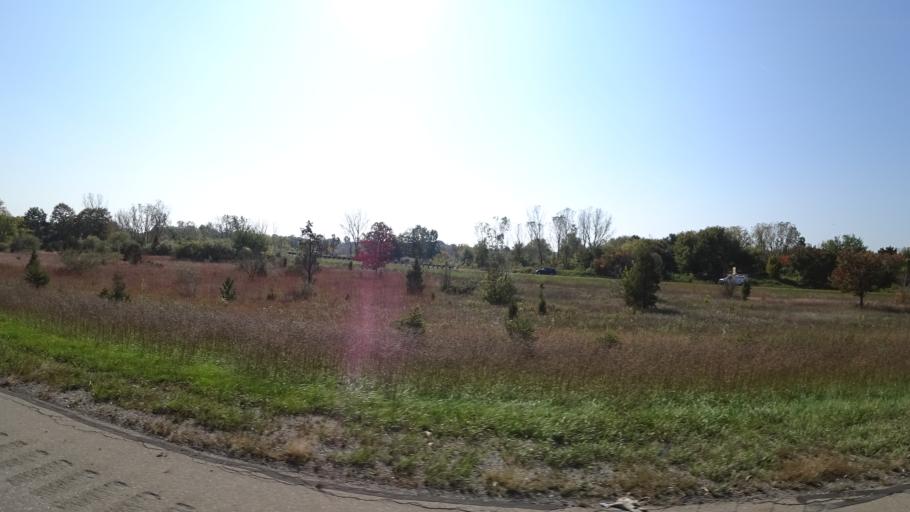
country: US
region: Michigan
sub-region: Washtenaw County
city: Chelsea
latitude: 42.2966
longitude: -84.0903
